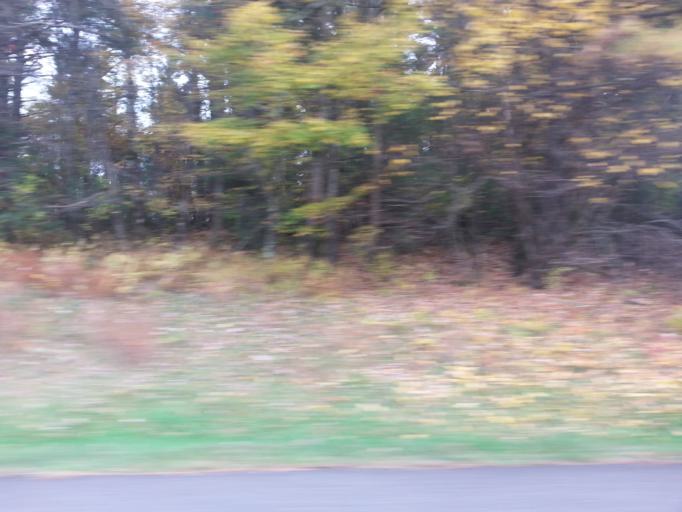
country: US
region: North Carolina
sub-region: Ashe County
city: Jefferson
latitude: 36.2908
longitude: -81.3735
